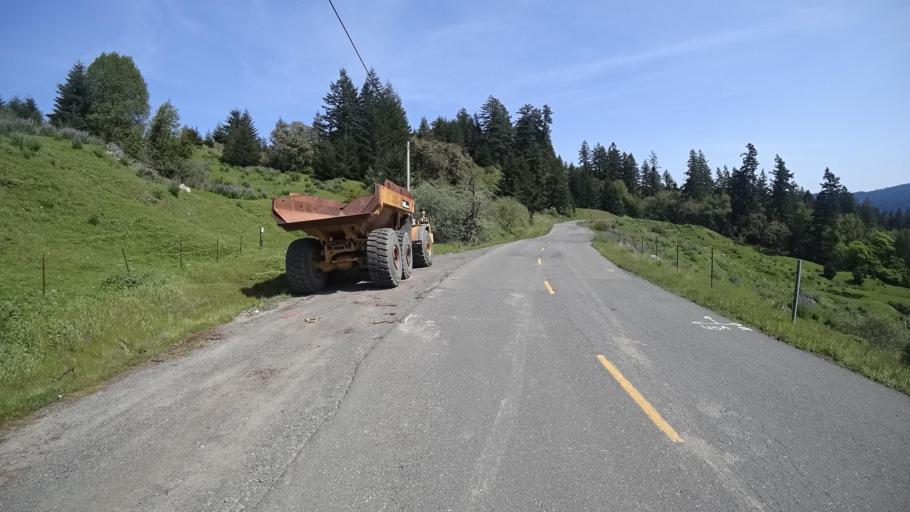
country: US
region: California
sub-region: Humboldt County
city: Redway
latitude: 40.4057
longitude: -123.7476
